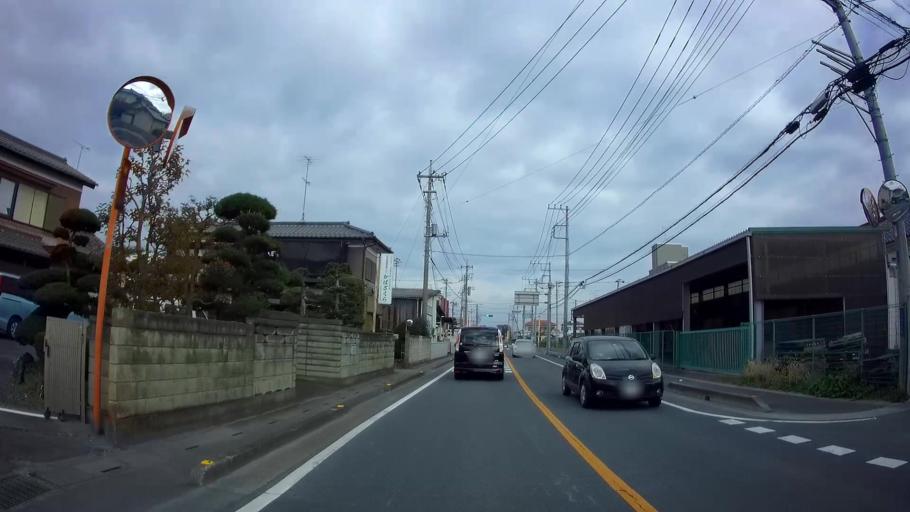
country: JP
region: Saitama
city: Okegawa
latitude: 36.0172
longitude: 139.5170
